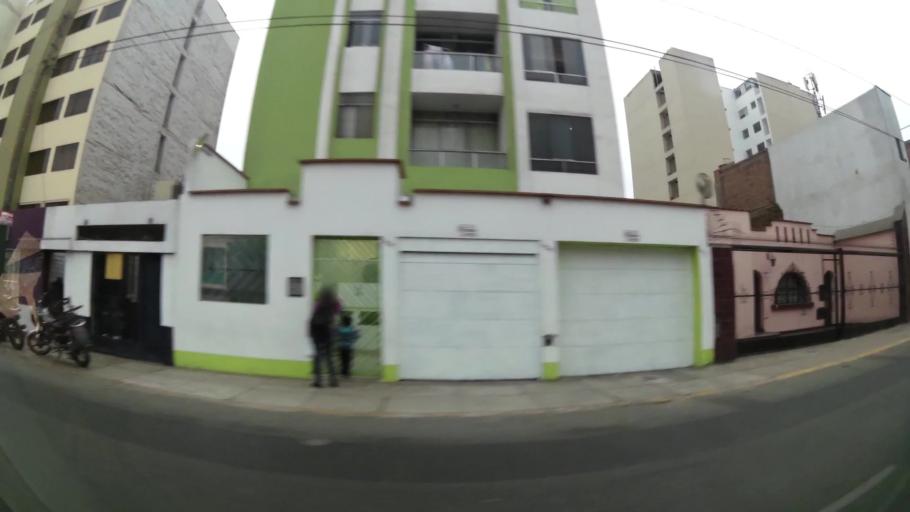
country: PE
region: Lima
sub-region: Lima
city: San Isidro
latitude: -12.0856
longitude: -77.0682
